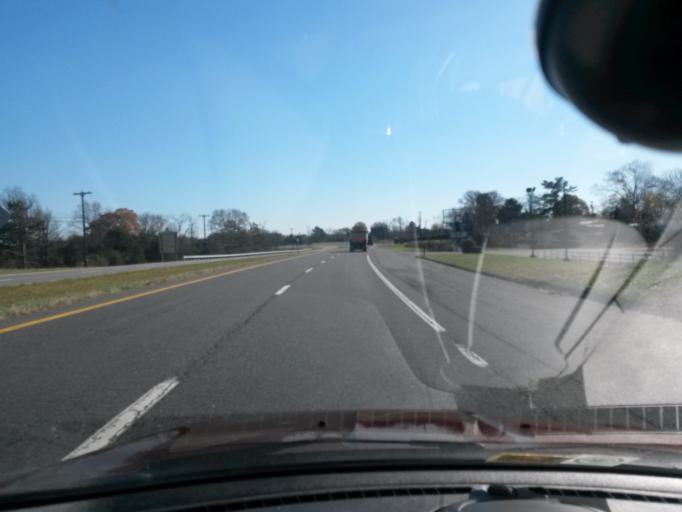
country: US
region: Virginia
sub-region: City of Bedford
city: Bedford
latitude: 37.3222
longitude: -79.4933
